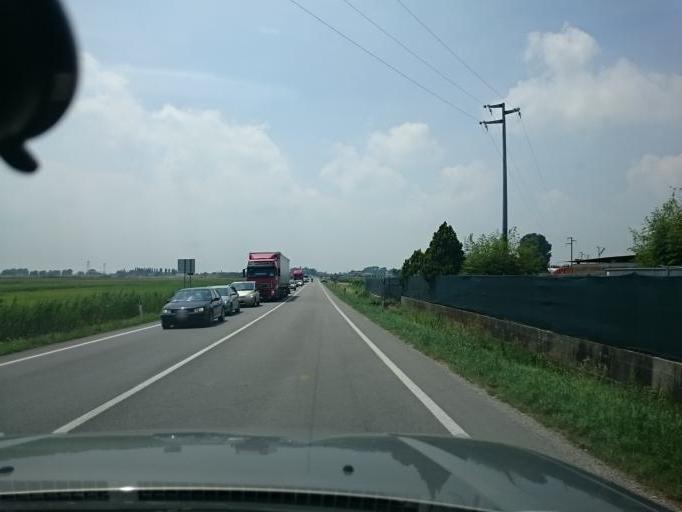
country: IT
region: Veneto
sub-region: Provincia di Padova
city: Codevigo
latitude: 45.2419
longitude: 12.1242
